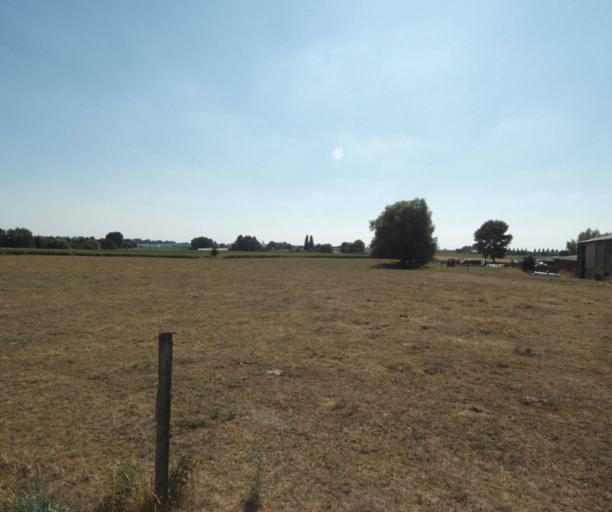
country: FR
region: Nord-Pas-de-Calais
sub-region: Departement du Nord
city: Bousbecque
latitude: 50.7596
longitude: 3.0887
